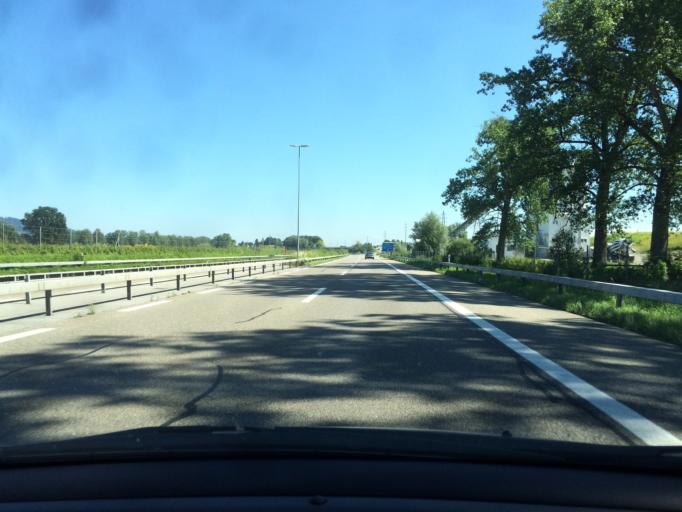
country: CH
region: Saint Gallen
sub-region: Wahlkreis Rheintal
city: Diepoldsau
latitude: 47.3855
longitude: 9.6406
